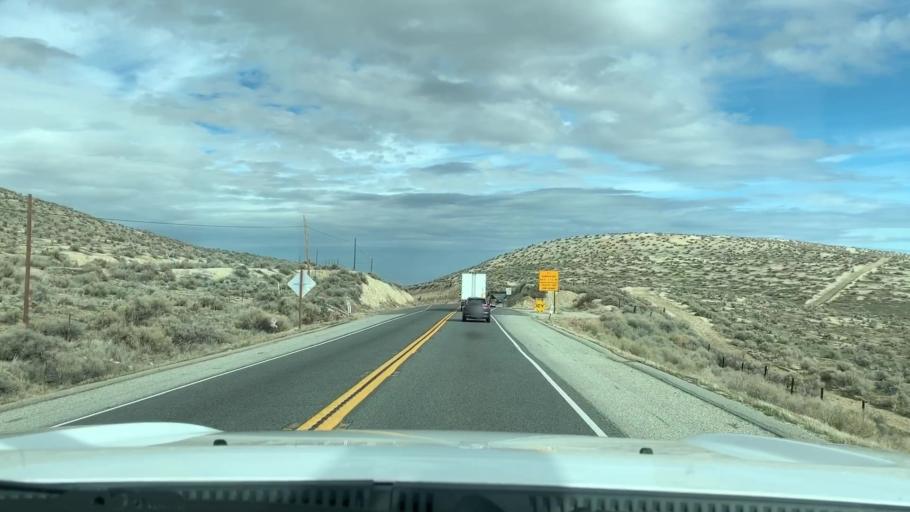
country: US
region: California
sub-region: Kern County
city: South Taft
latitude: 35.1317
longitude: -119.4029
